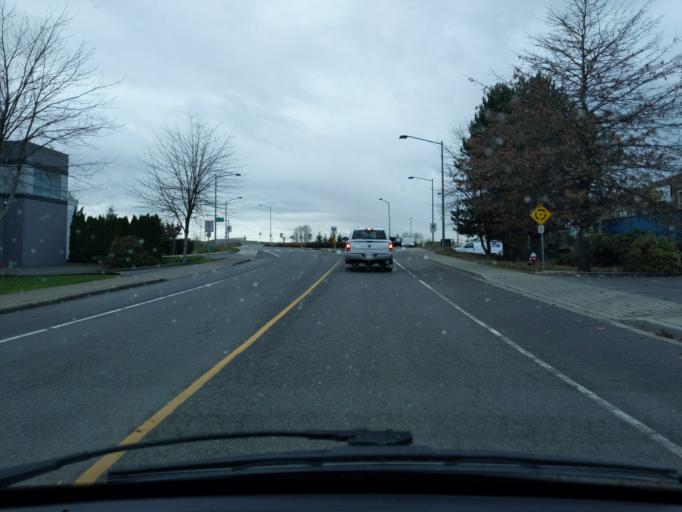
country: CA
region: British Columbia
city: Pitt Meadows
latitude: 49.2094
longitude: -122.6660
